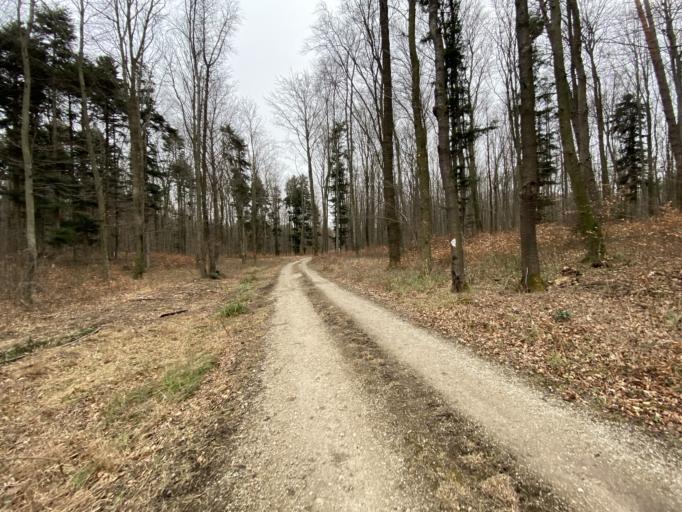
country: AT
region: Lower Austria
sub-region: Politischer Bezirk Modling
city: Gaaden
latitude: 48.0224
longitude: 16.2004
